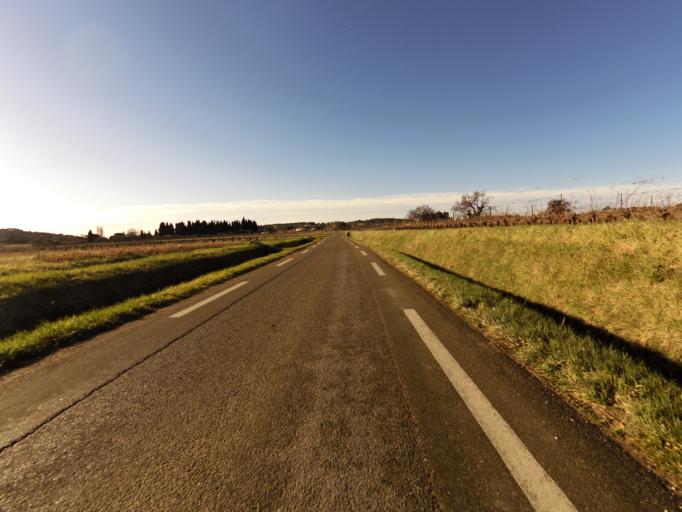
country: FR
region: Languedoc-Roussillon
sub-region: Departement du Gard
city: Aigues-Vives
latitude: 43.7489
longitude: 4.1841
